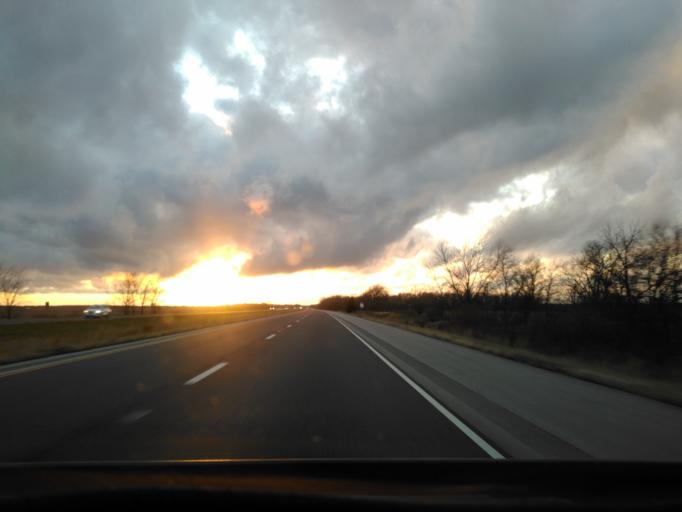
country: US
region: Illinois
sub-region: Fayette County
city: Saint Elmo
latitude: 38.9929
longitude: -88.9237
